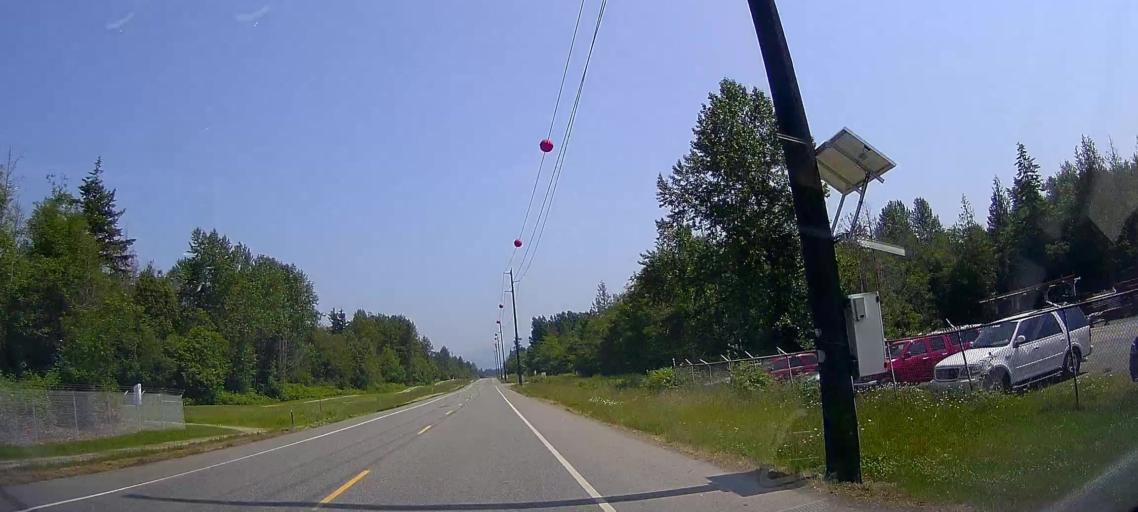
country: US
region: Washington
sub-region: Skagit County
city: Mount Vernon
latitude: 48.4576
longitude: -122.4317
